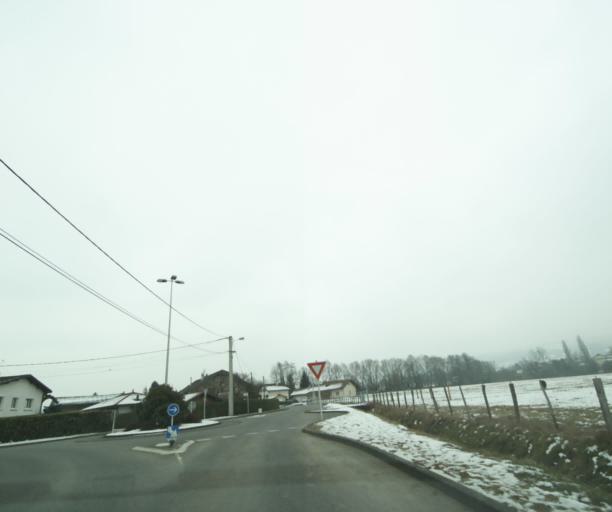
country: FR
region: Rhone-Alpes
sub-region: Departement de la Haute-Savoie
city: Reignier-Esery
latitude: 46.1333
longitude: 6.2793
